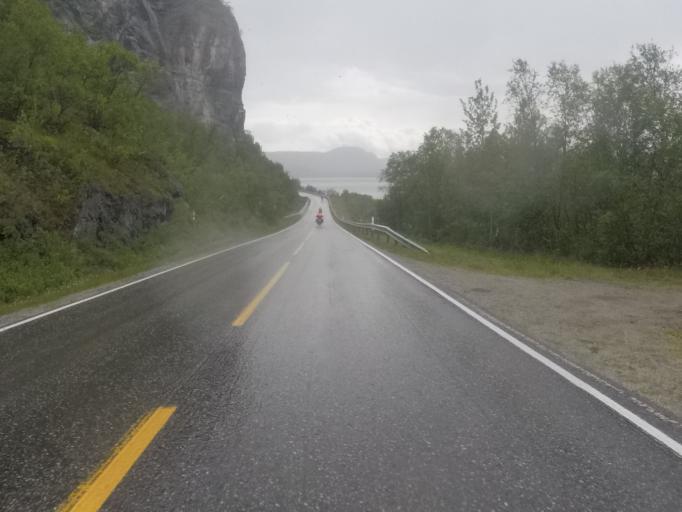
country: NO
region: Finnmark Fylke
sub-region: Porsanger
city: Lakselv
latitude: 69.8576
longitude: 25.0499
